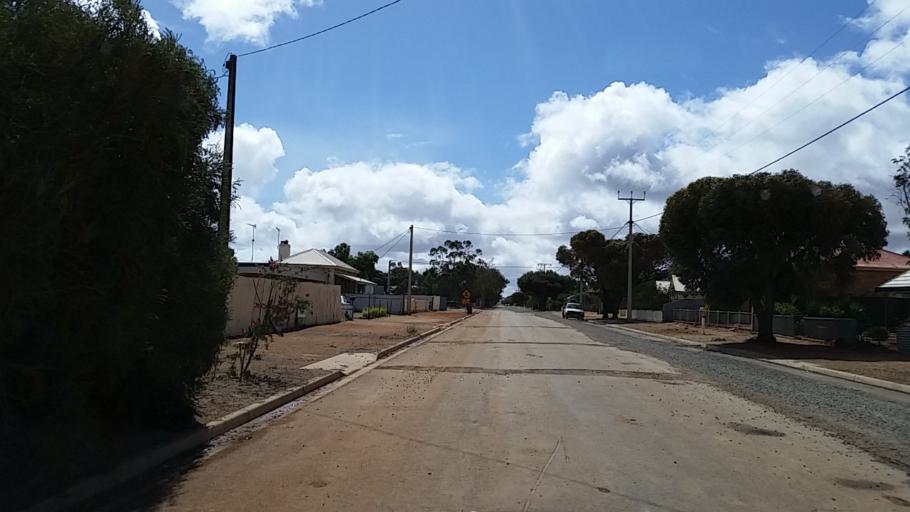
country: AU
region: South Australia
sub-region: Peterborough
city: Peterborough
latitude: -32.9753
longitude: 138.8304
